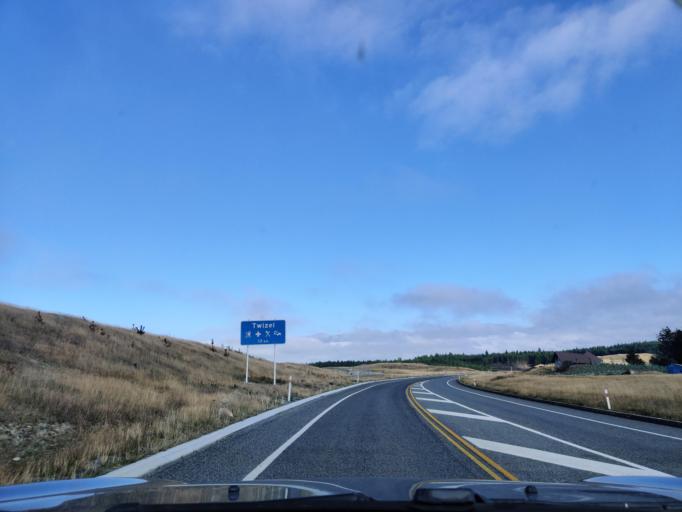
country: NZ
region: Canterbury
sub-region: Timaru District
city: Pleasant Point
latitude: -44.1910
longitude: 170.1410
